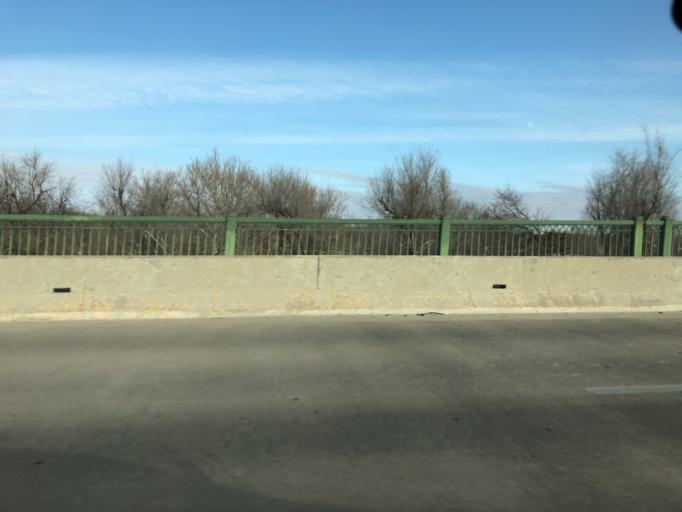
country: US
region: Kansas
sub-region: Reno County
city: Hutchinson
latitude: 38.0573
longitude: -97.9436
